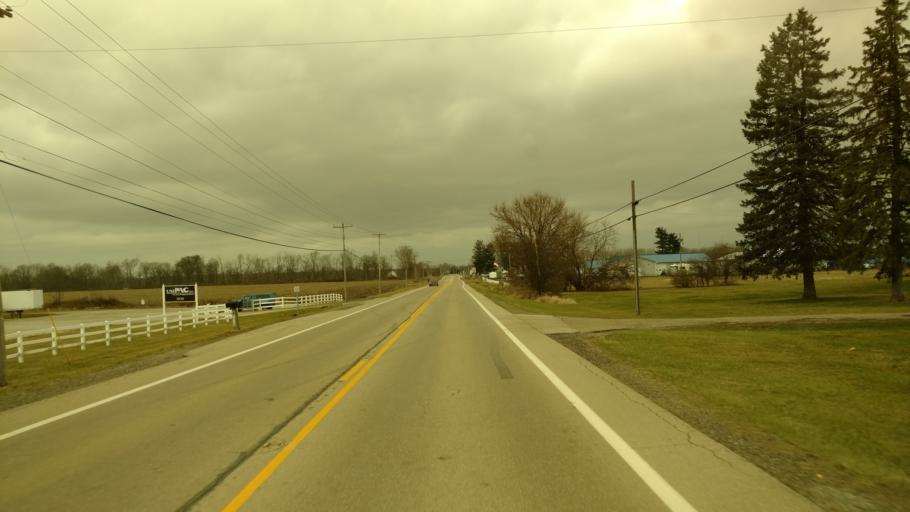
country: US
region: Ohio
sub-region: Licking County
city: Hebron
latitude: 39.9578
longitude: -82.5372
